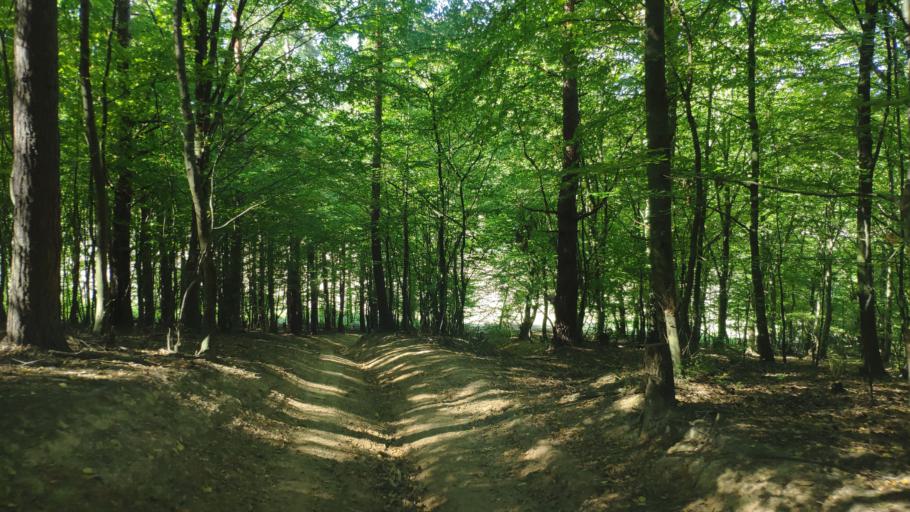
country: SK
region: Presovsky
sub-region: Okres Presov
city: Presov
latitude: 48.9796
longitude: 21.1412
